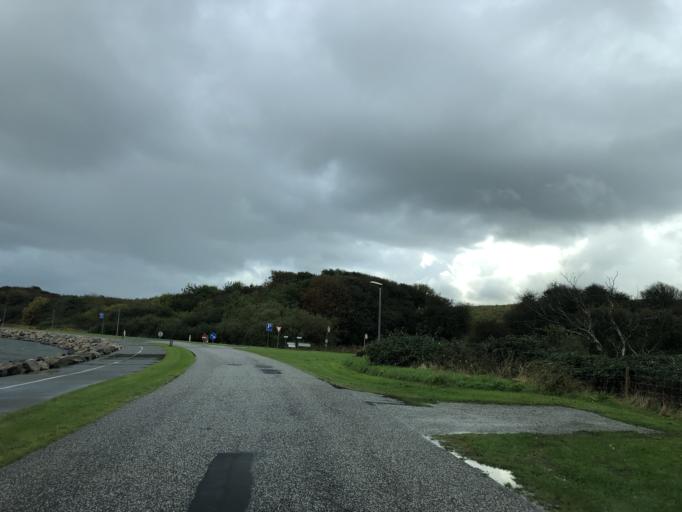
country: DK
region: Central Jutland
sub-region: Lemvig Kommune
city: Lemvig
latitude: 56.5625
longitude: 8.2944
